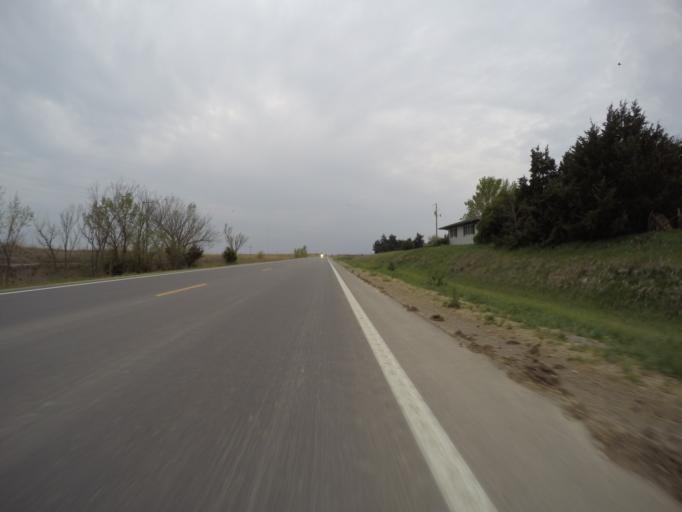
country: US
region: Kansas
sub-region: Pottawatomie County
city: Westmoreland
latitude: 39.3461
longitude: -96.5198
